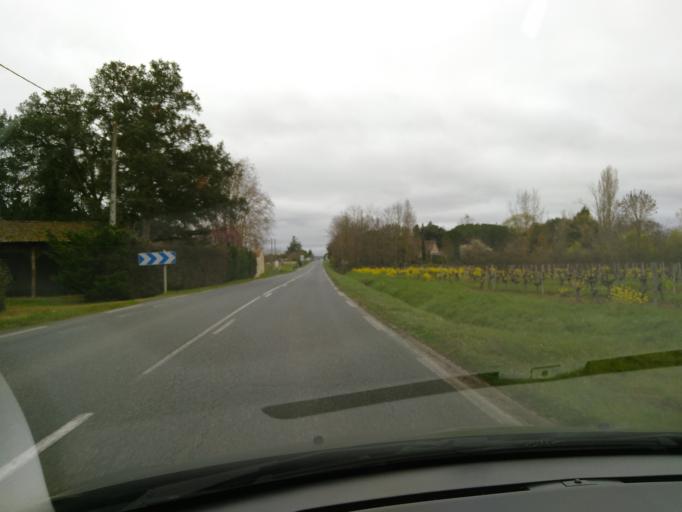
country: FR
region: Aquitaine
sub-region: Departement de la Dordogne
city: Monbazillac
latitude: 44.8149
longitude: 0.5061
